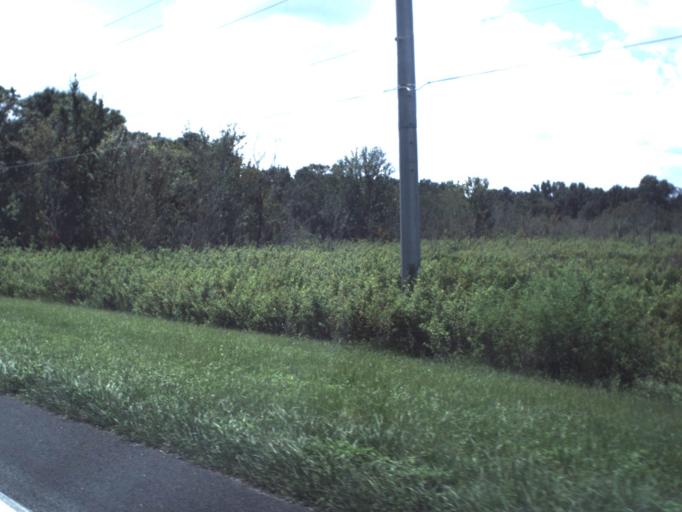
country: US
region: Florida
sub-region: Hillsborough County
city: Plant City
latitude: 28.0799
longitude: -82.1386
